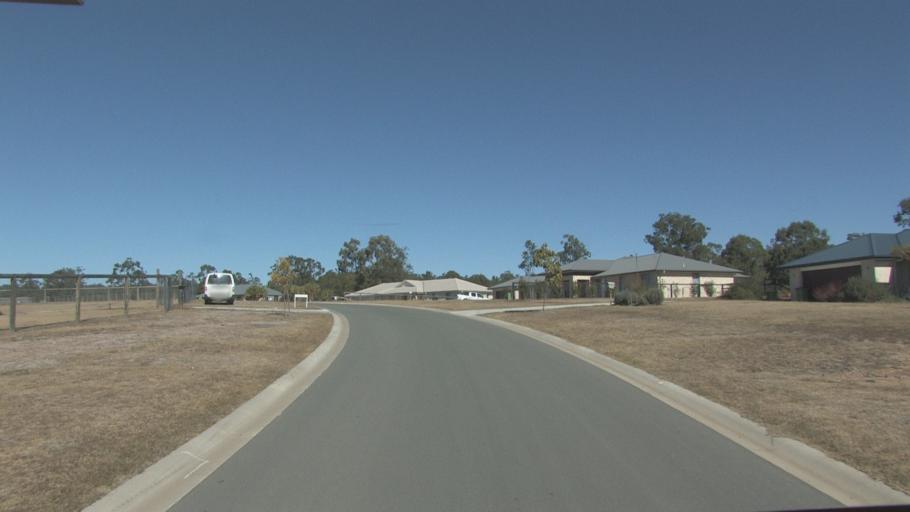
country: AU
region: Queensland
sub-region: Logan
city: Cedar Vale
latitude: -27.8668
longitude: 153.0425
